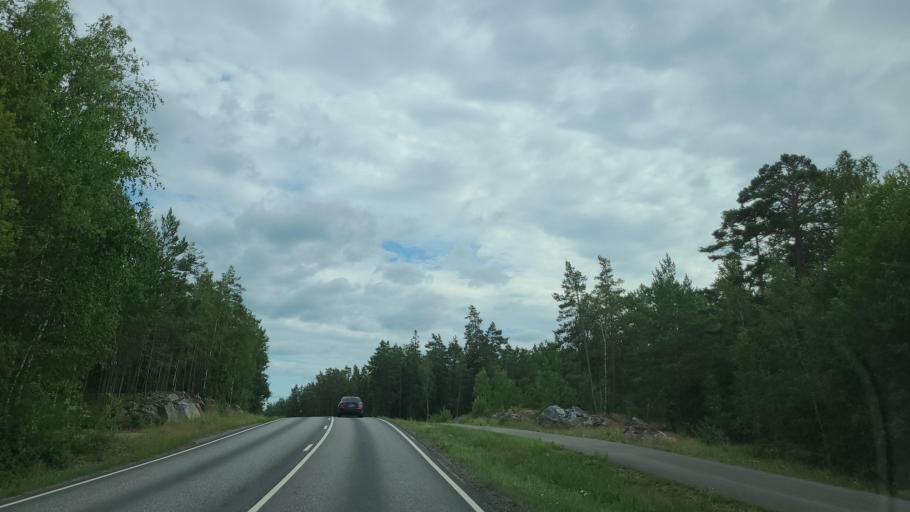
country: FI
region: Varsinais-Suomi
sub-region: Turku
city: Rymaettylae
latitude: 60.3966
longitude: 21.8998
